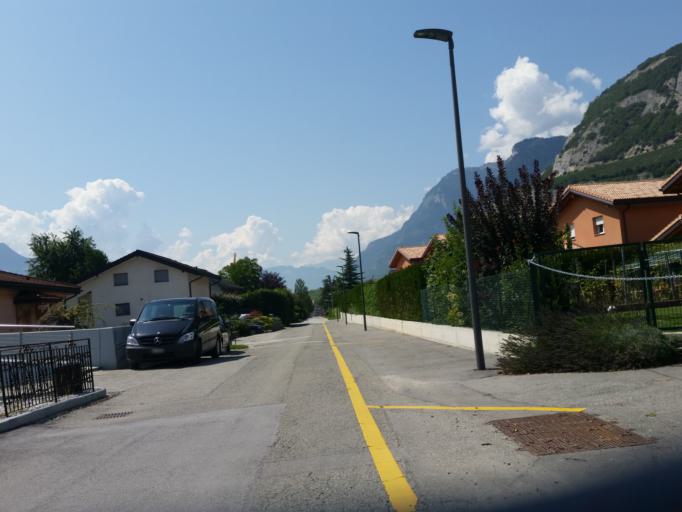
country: CH
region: Valais
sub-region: Conthey District
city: Ardon
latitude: 46.2106
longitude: 7.2627
